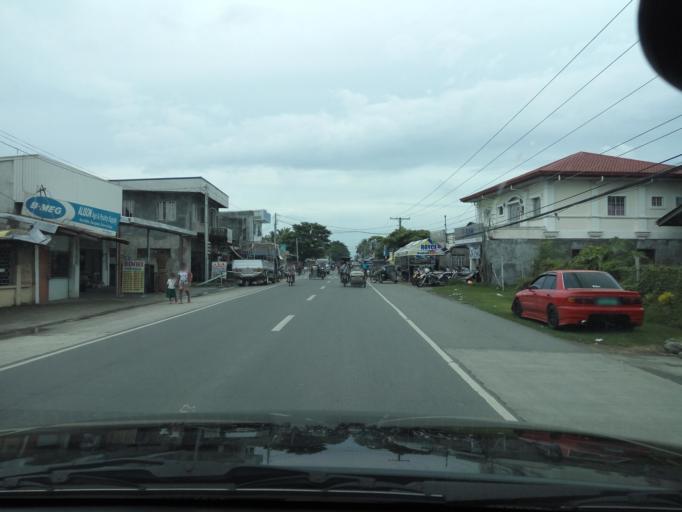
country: PH
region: Central Luzon
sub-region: Province of Nueva Ecija
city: Concepcion
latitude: 15.4491
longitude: 120.7999
